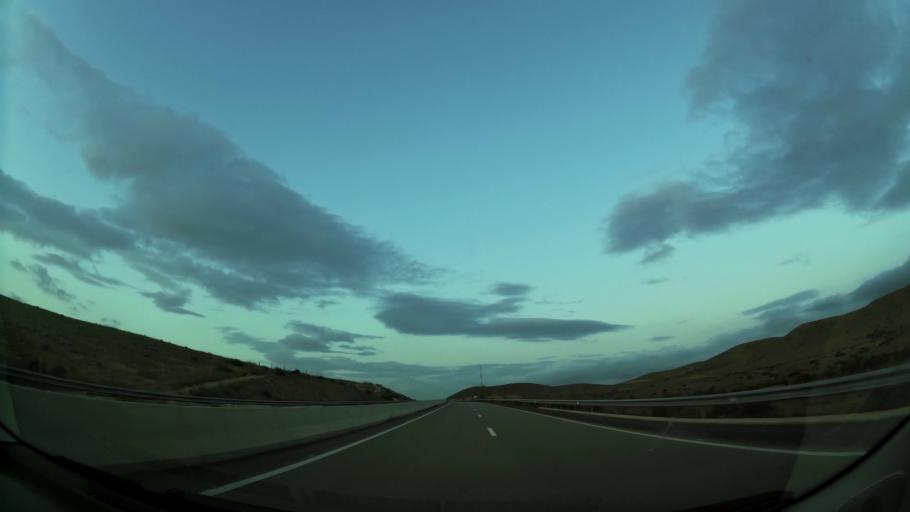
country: MA
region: Oriental
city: El Aioun
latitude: 34.6062
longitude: -2.5898
